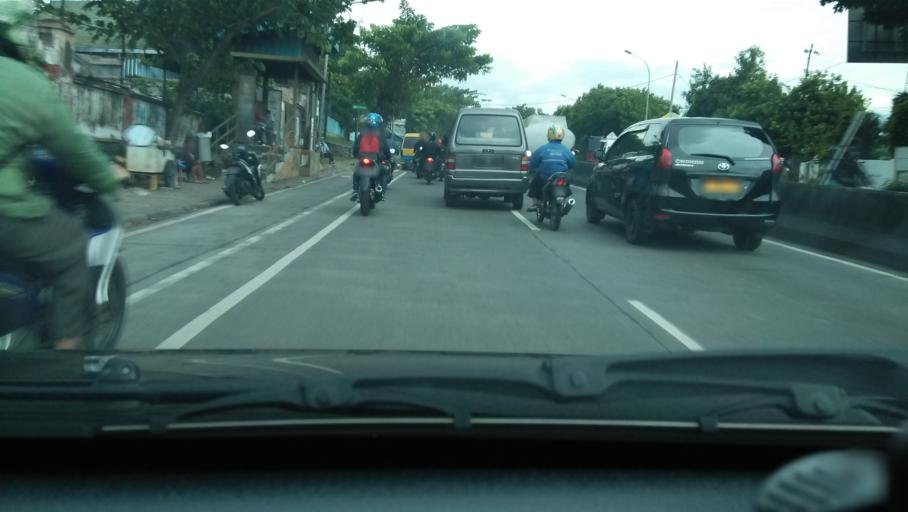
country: ID
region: Central Java
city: Ungaran
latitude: -7.0740
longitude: 110.4113
